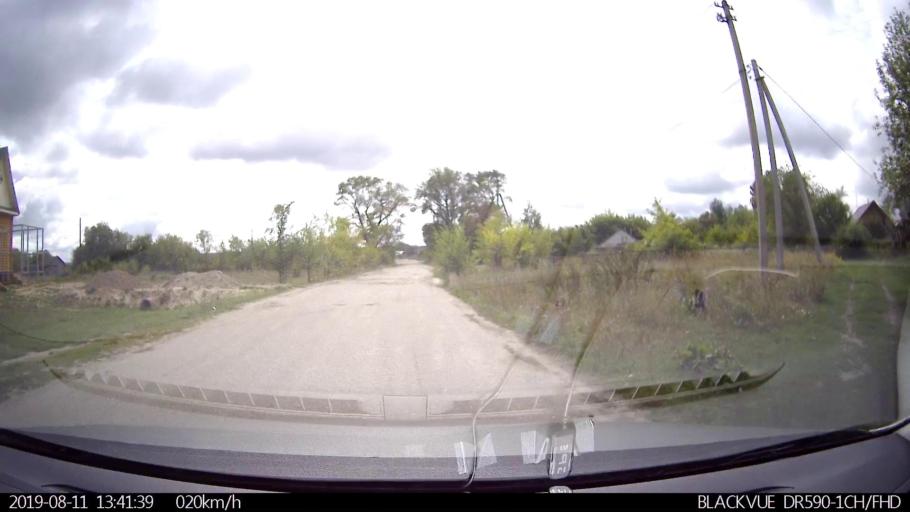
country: RU
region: Ulyanovsk
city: Ignatovka
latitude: 53.8574
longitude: 47.5758
